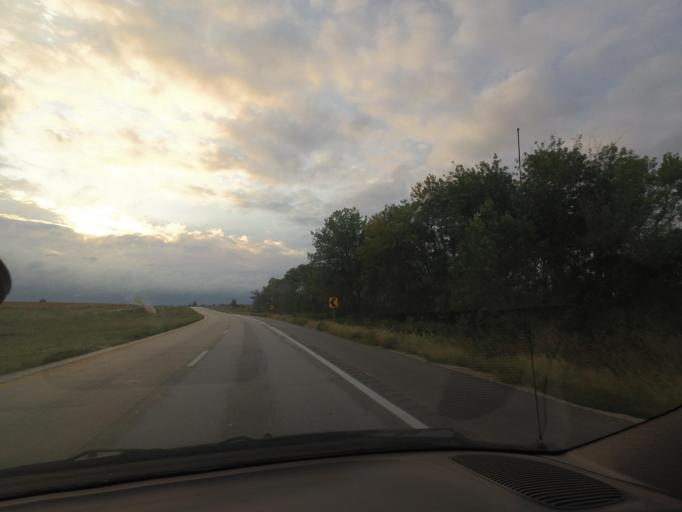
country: US
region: Missouri
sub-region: Shelby County
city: Shelbina
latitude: 39.6890
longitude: -92.0195
